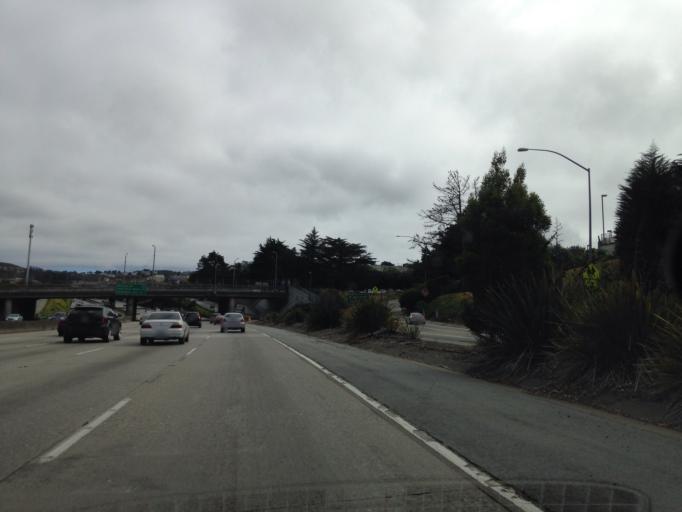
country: US
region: California
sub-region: San Mateo County
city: Daly City
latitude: 37.7244
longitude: -122.4474
